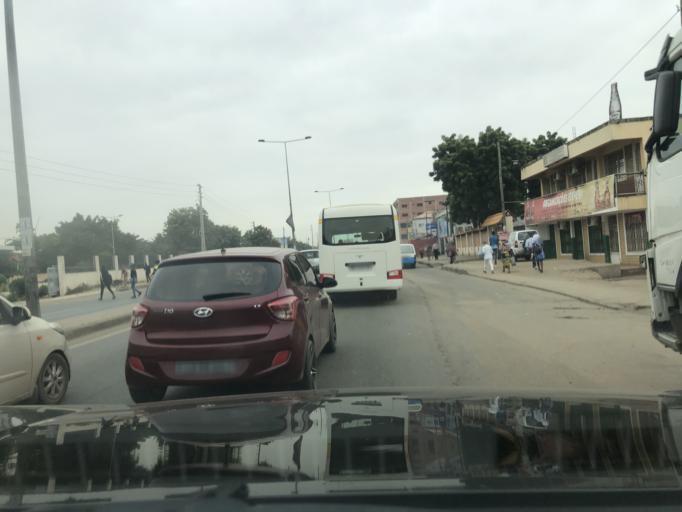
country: AO
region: Luanda
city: Luanda
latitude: -8.8570
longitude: 13.2811
